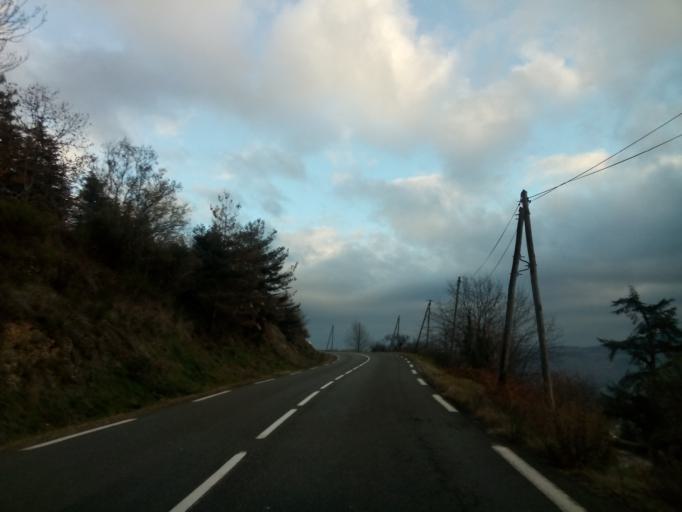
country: FR
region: Rhone-Alpes
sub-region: Departement de la Loire
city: Bourg-Argental
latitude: 45.3071
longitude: 4.5785
